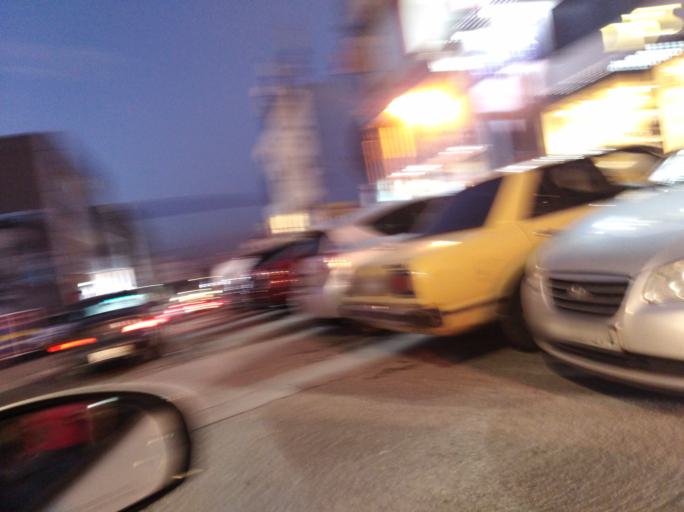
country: JO
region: Amman
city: Wadi as Sir
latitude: 31.9568
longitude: 35.8653
